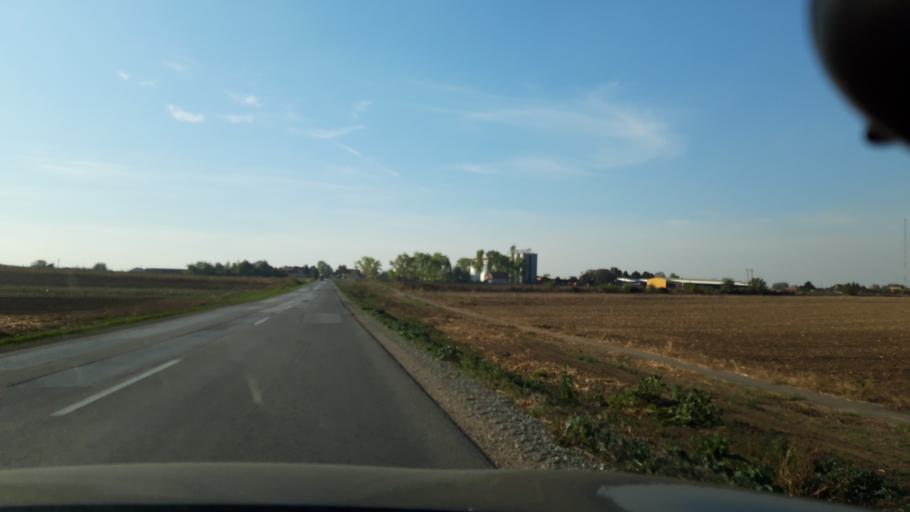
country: RS
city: Putinci
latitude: 44.9991
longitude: 19.9458
